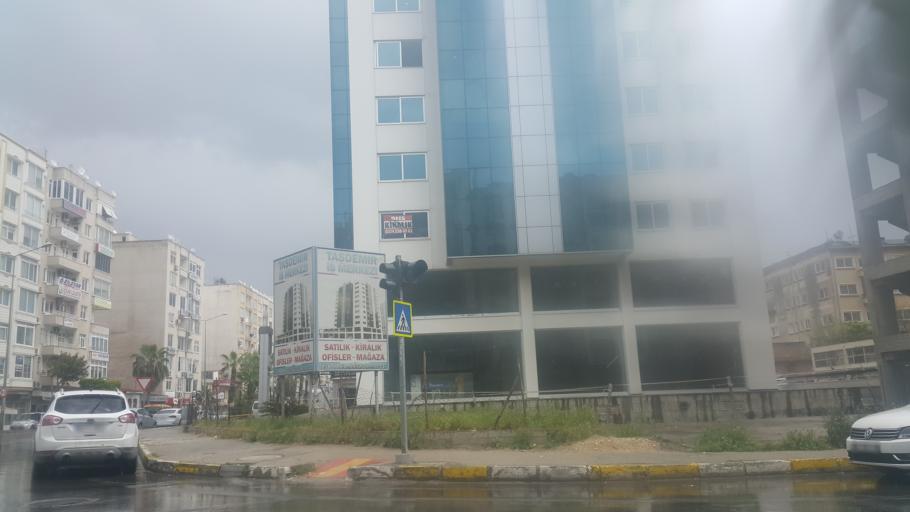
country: TR
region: Mersin
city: Mercin
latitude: 36.8036
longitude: 34.6316
